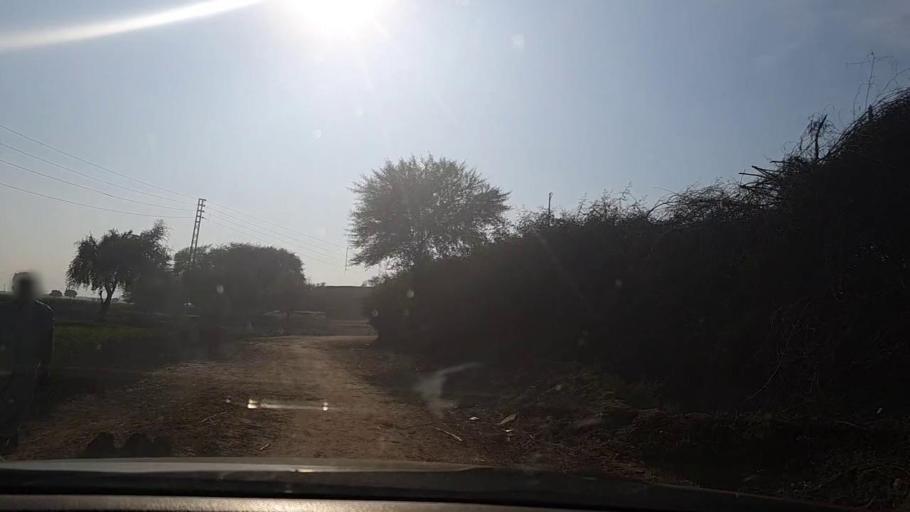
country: PK
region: Sindh
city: Sehwan
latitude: 26.2990
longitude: 68.0047
